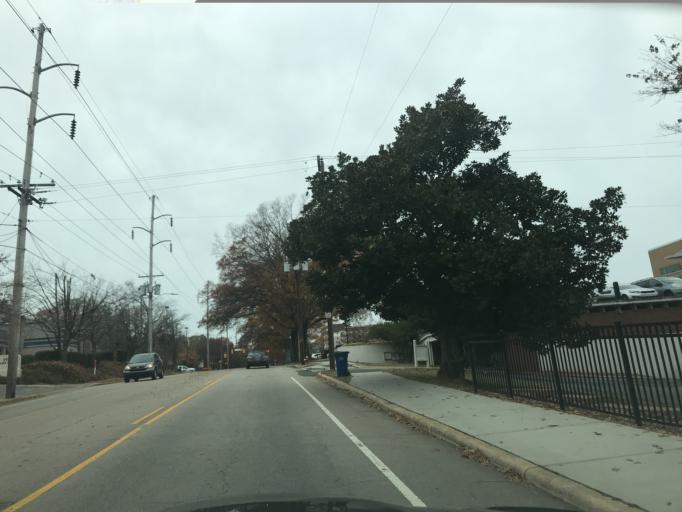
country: US
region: North Carolina
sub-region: Wake County
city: West Raleigh
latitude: 35.7891
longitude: -78.6575
